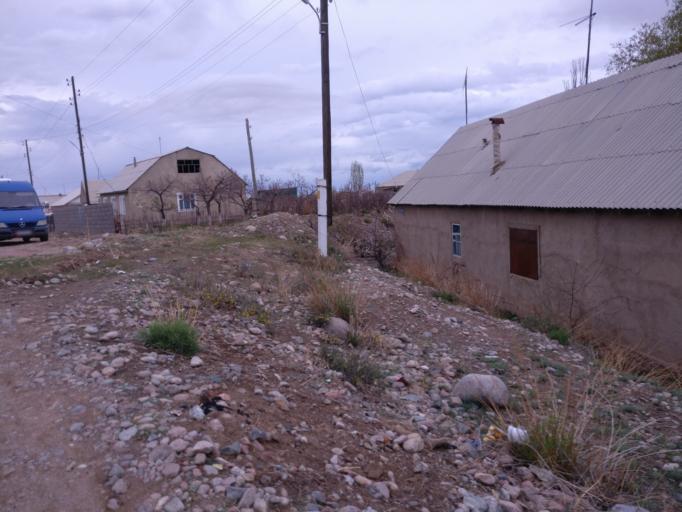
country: KG
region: Ysyk-Koel
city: Bokombayevskoye
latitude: 42.1115
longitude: 76.9813
